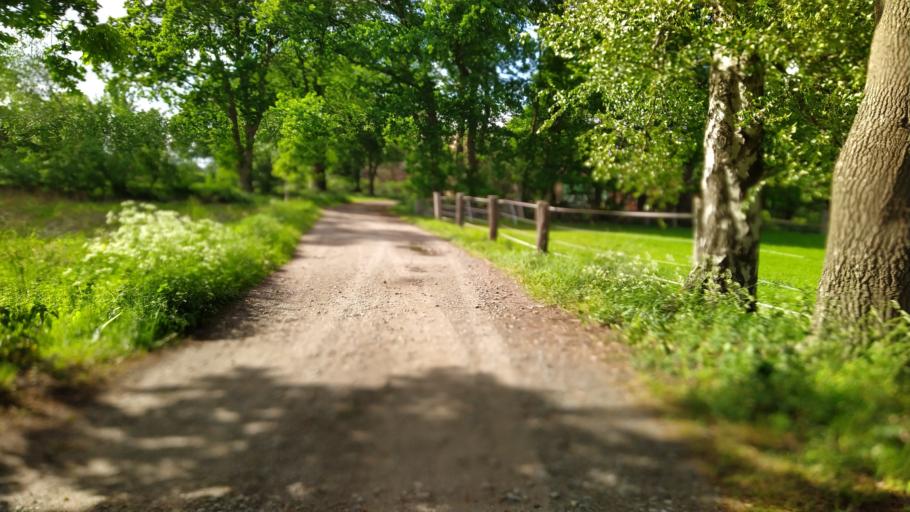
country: DE
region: Lower Saxony
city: Brest
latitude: 53.4634
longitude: 9.4010
